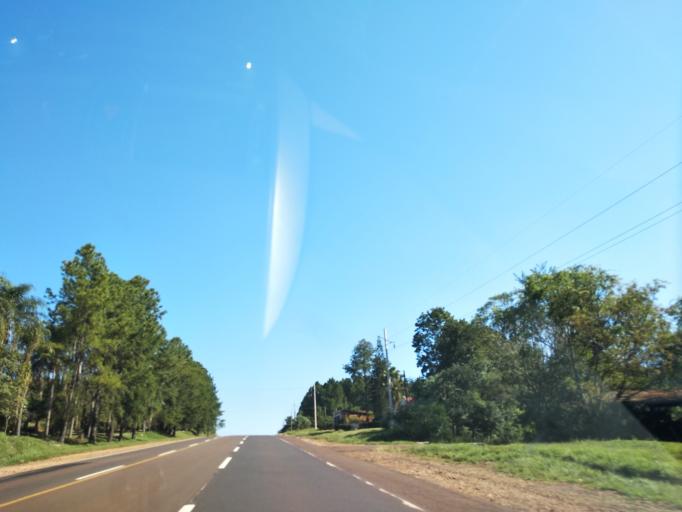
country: AR
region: Misiones
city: Capiovi
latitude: -26.8983
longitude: -55.0589
